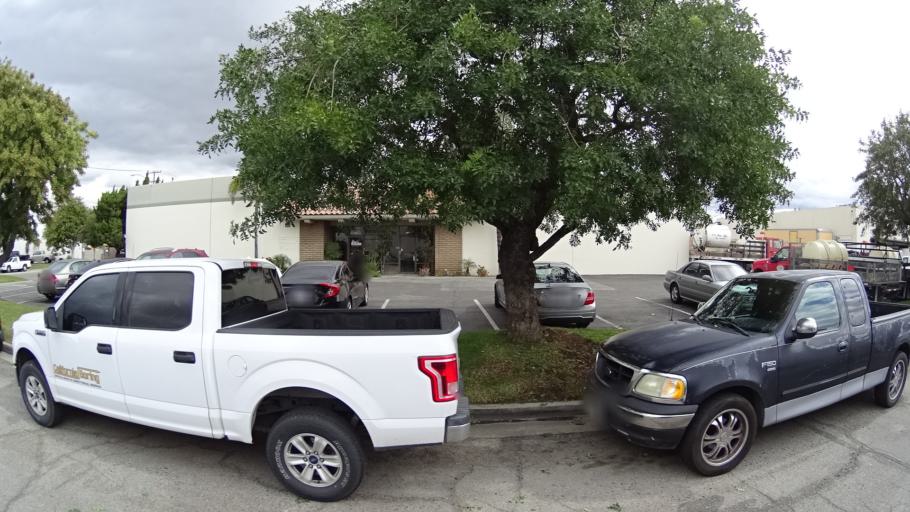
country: US
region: California
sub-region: Orange County
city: Placentia
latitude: 33.8539
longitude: -117.8599
